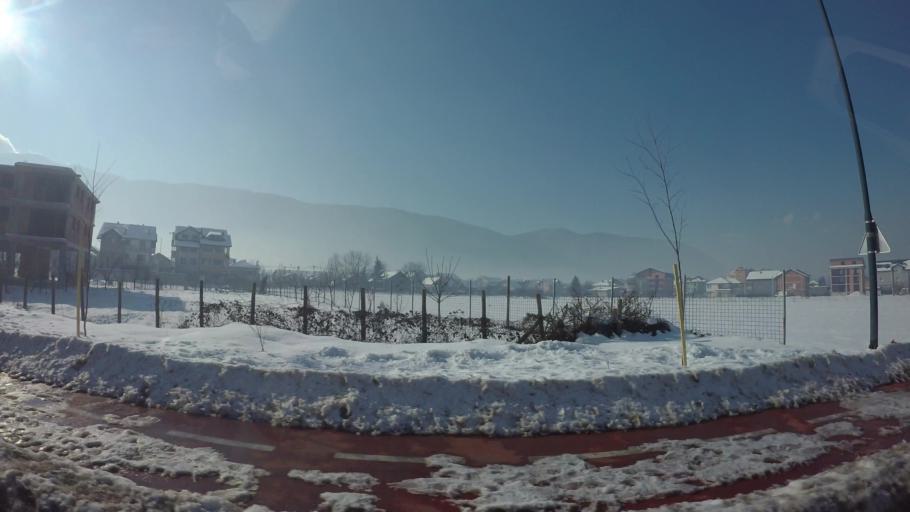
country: BA
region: Federation of Bosnia and Herzegovina
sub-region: Kanton Sarajevo
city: Sarajevo
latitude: 43.8122
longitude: 18.3096
